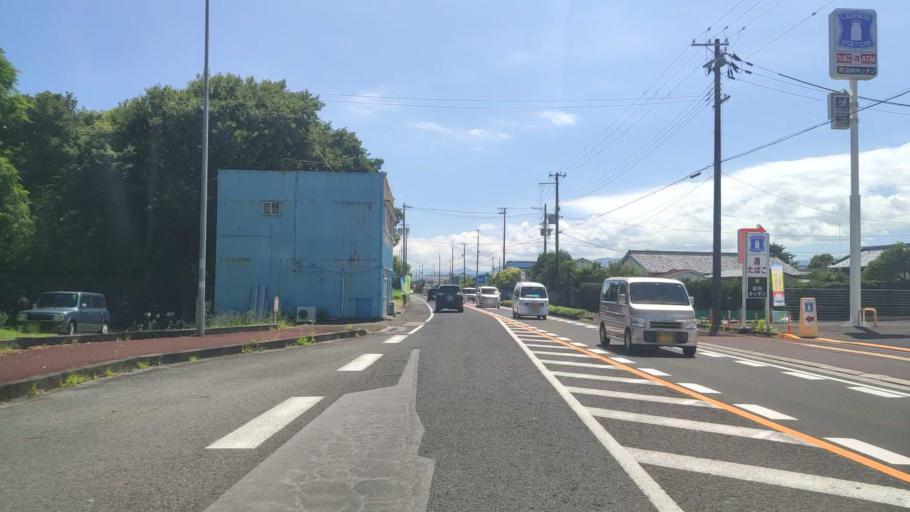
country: JP
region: Wakayama
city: Shingu
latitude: 33.8747
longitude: 136.0882
